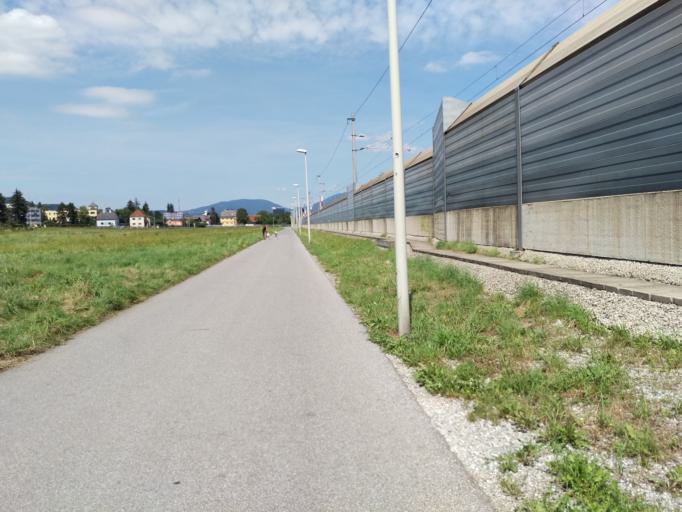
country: AT
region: Styria
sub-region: Graz Stadt
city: Wetzelsdorf
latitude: 47.0512
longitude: 15.4192
